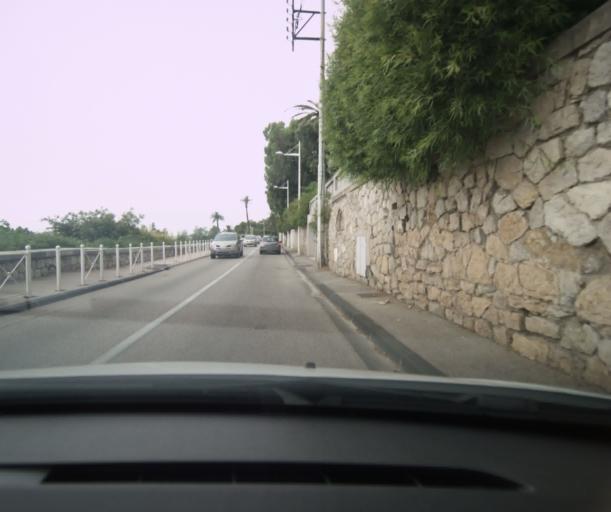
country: FR
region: Provence-Alpes-Cote d'Azur
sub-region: Departement du Var
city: Toulon
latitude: 43.1086
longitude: 5.9493
